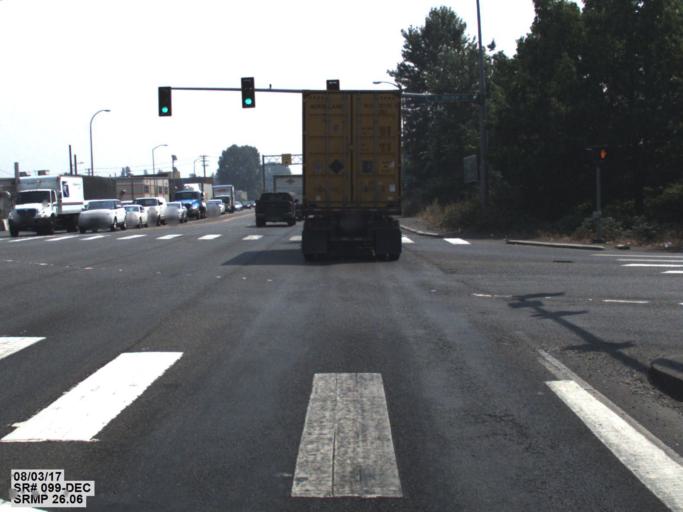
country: US
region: Washington
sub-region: King County
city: White Center
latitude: 47.5345
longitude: -122.3324
